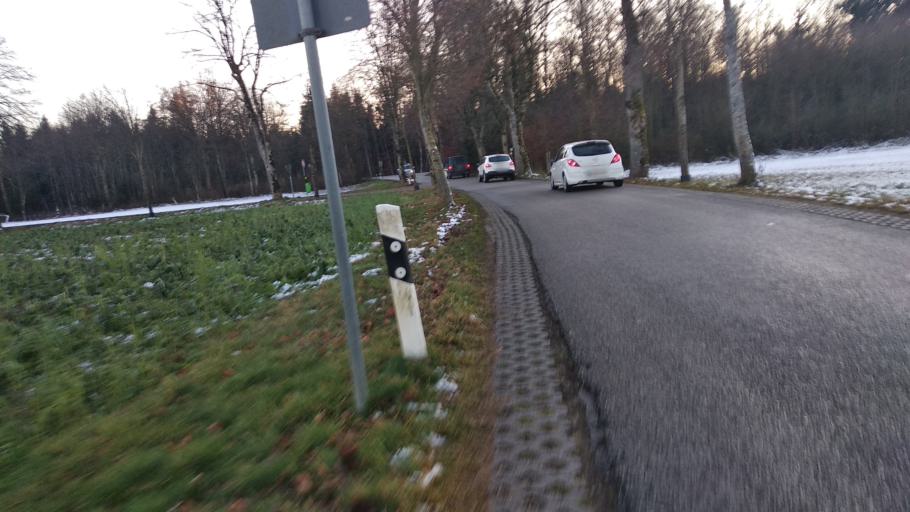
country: DE
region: Bavaria
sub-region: Upper Bavaria
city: Grasbrunn
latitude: 48.0731
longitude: 11.7734
